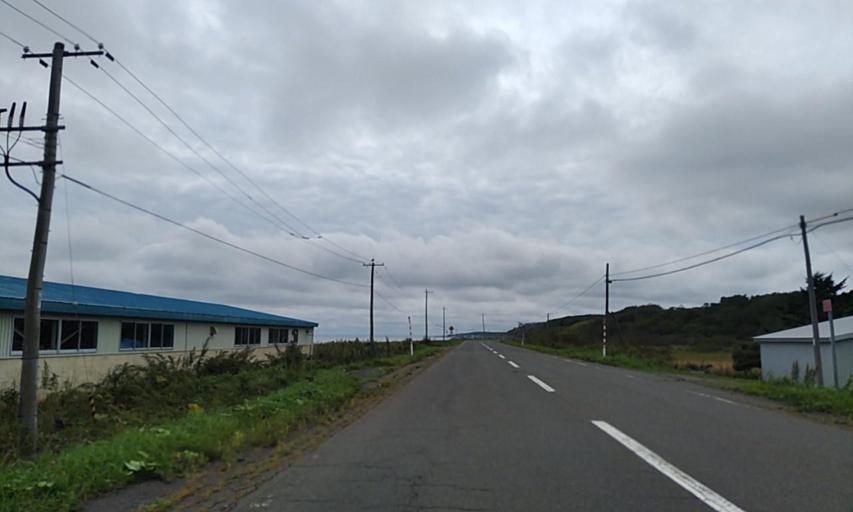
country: JP
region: Hokkaido
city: Shibetsu
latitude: 43.5109
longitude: 145.2449
